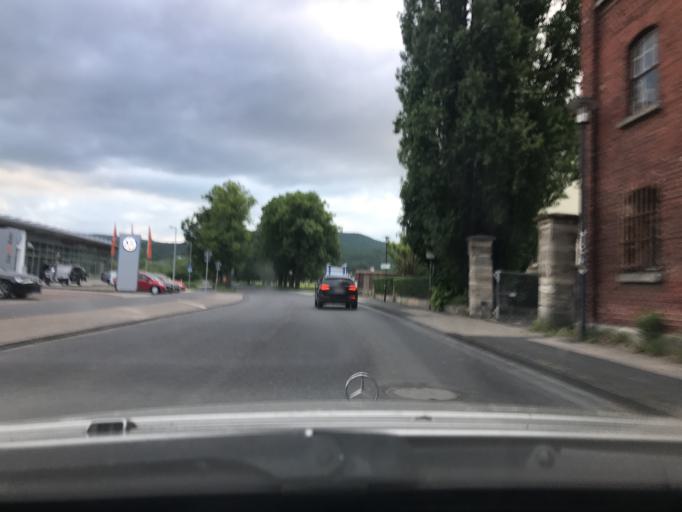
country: DE
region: Hesse
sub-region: Regierungsbezirk Kassel
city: Eschwege
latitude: 51.1925
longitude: 10.0580
